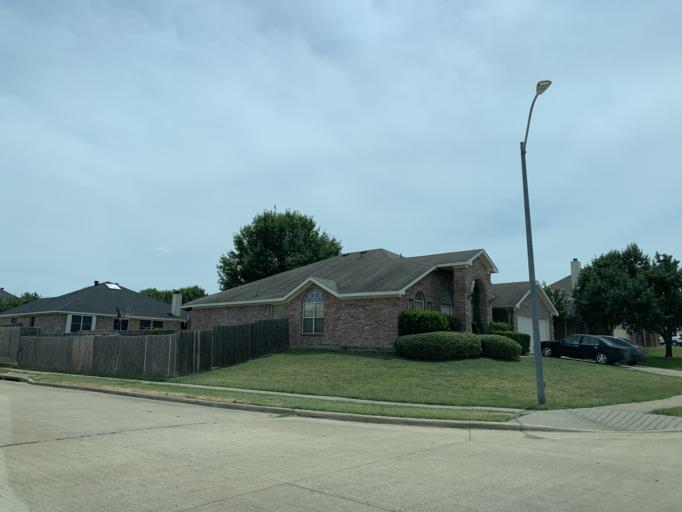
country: US
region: Texas
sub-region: Dallas County
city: Grand Prairie
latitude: 32.6638
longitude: -97.0235
